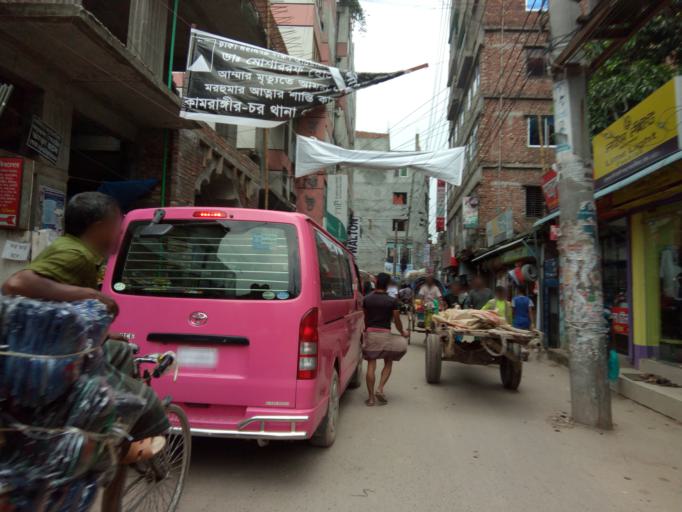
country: BD
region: Dhaka
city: Azimpur
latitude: 23.7197
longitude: 90.3736
